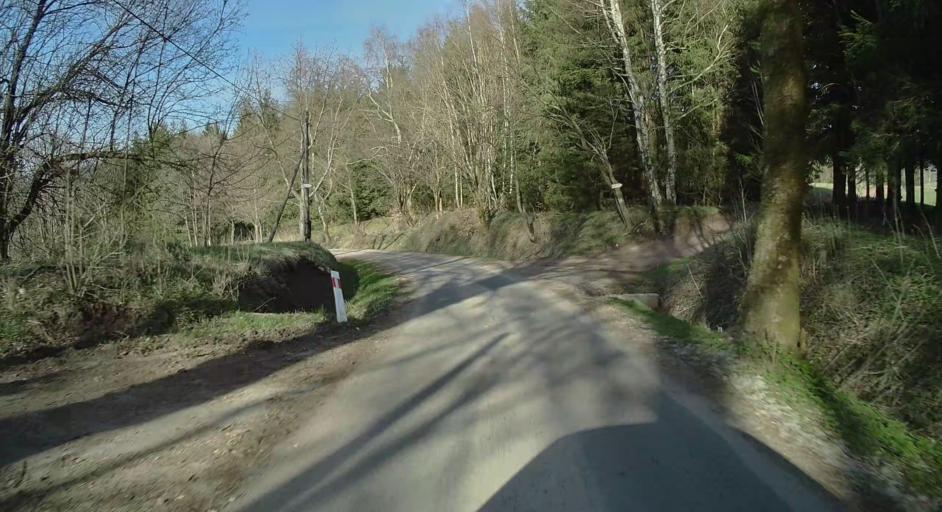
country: PL
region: Lower Silesian Voivodeship
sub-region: Powiat klodzki
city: Lewin Klodzki
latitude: 50.3762
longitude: 16.2893
